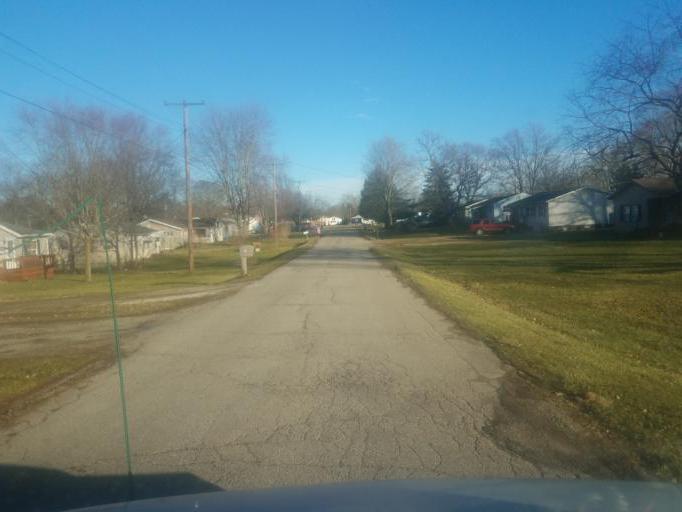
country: US
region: Ohio
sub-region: Richland County
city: Ontario
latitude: 40.7935
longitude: -82.5547
